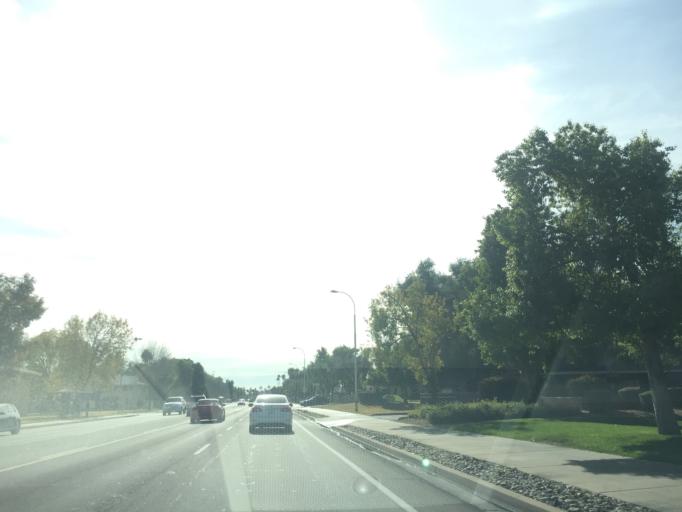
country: US
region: Arizona
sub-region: Maricopa County
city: Guadalupe
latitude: 33.3815
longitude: -111.9395
